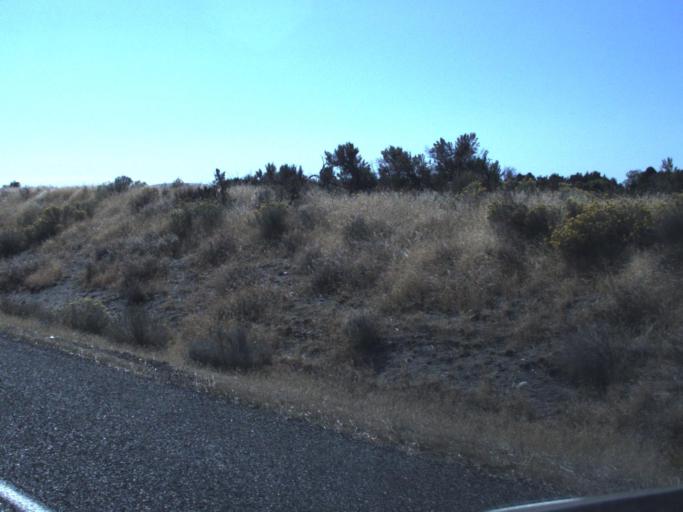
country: US
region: Washington
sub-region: Benton County
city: West Richland
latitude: 46.3732
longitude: -119.4044
